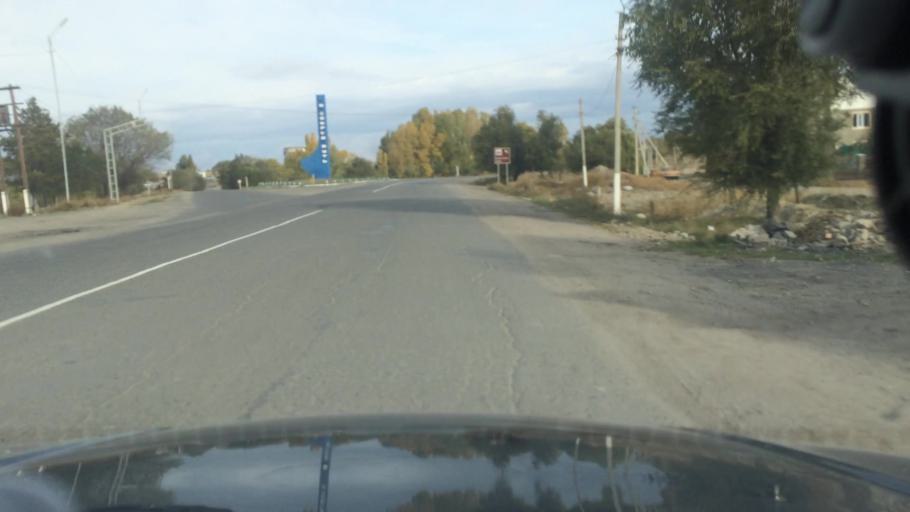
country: KG
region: Ysyk-Koel
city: Karakol
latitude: 42.5316
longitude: 78.3824
